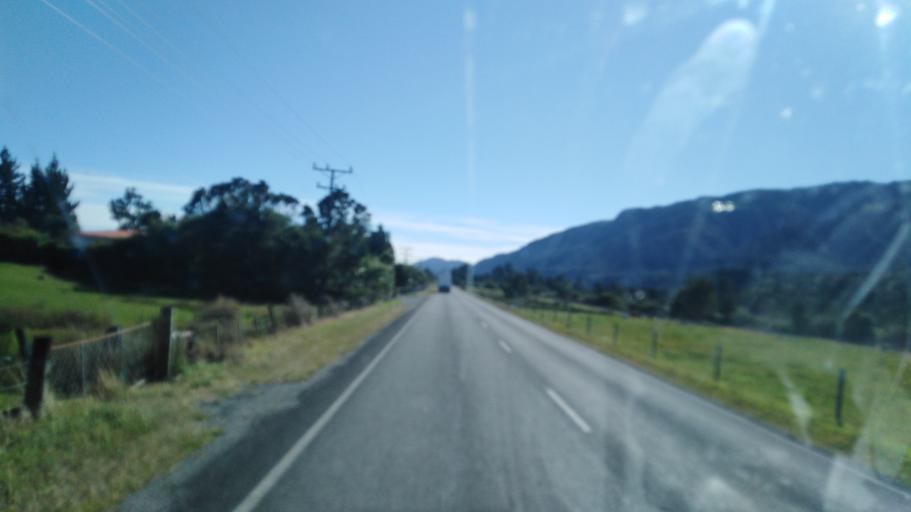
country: NZ
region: West Coast
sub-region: Buller District
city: Westport
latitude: -41.6730
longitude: 171.8021
